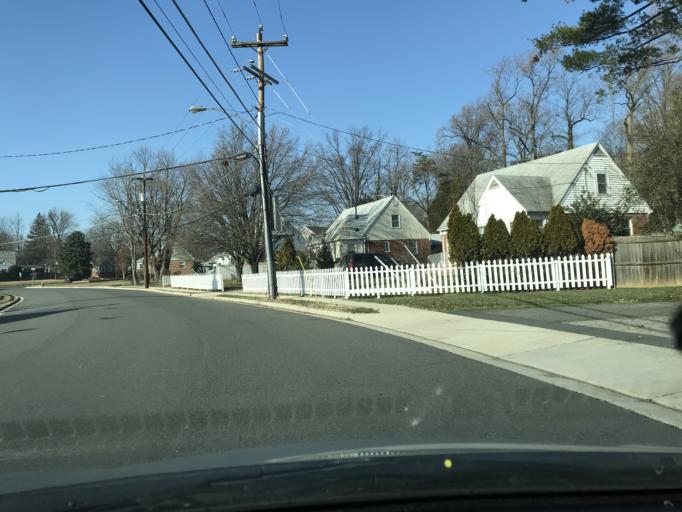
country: US
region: Virginia
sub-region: City of Fairfax
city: Fairfax
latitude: 38.8548
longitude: -77.3186
